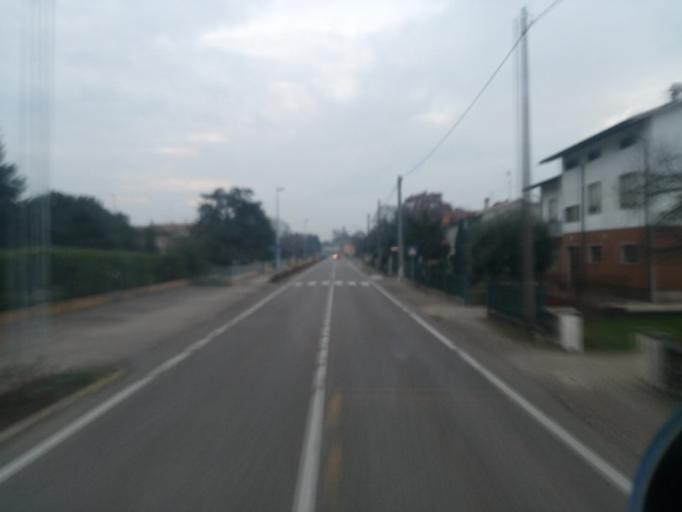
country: IT
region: Lombardy
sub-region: Provincia di Mantova
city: Roncoferraro
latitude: 45.1367
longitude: 10.9483
